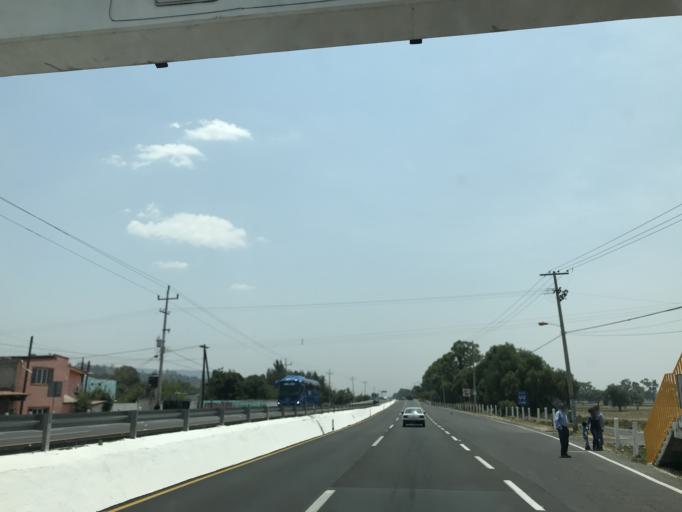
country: MX
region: Tlaxcala
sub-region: Ixtacuixtla de Mariano Matamoros
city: Santa Justina Ecatepec
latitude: 19.3286
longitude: -98.3490
